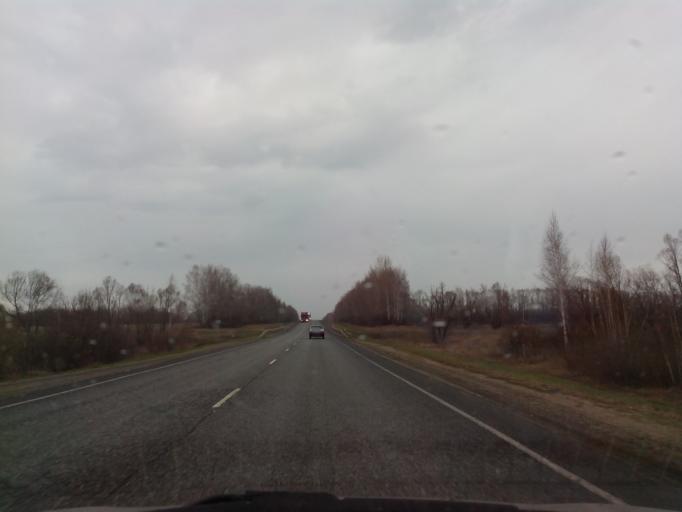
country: RU
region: Tambov
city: Pervomayskiy
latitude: 53.1470
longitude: 40.3742
